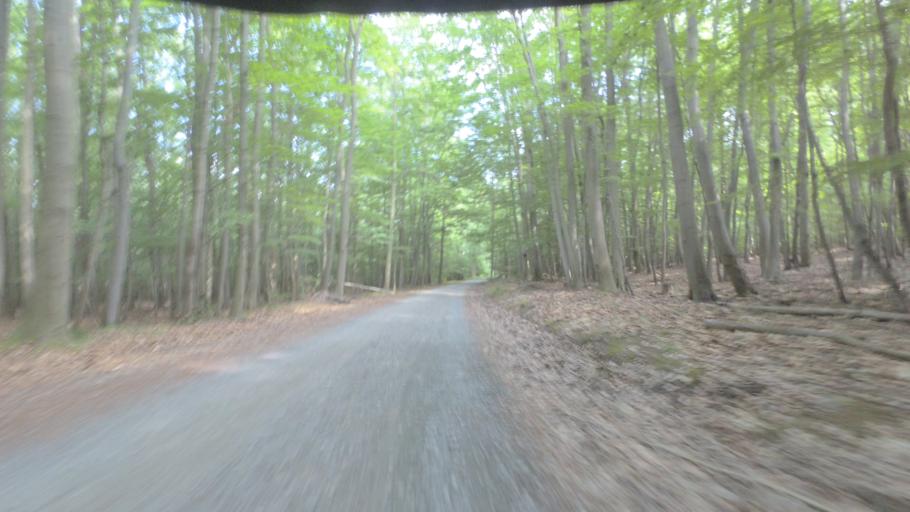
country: DE
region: Saxony-Anhalt
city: Stapelburg
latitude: 51.8795
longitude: 10.6586
